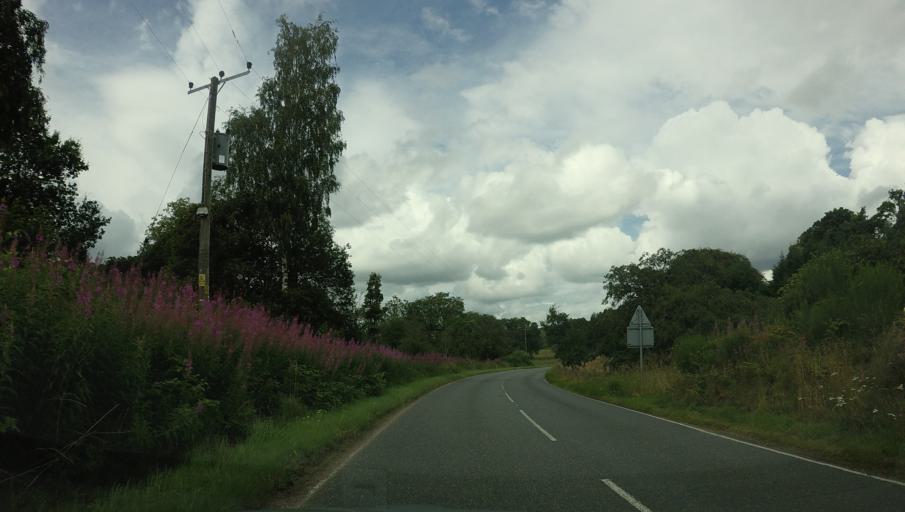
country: GB
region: Scotland
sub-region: Aberdeenshire
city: Banchory
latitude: 57.0585
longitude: -2.5488
